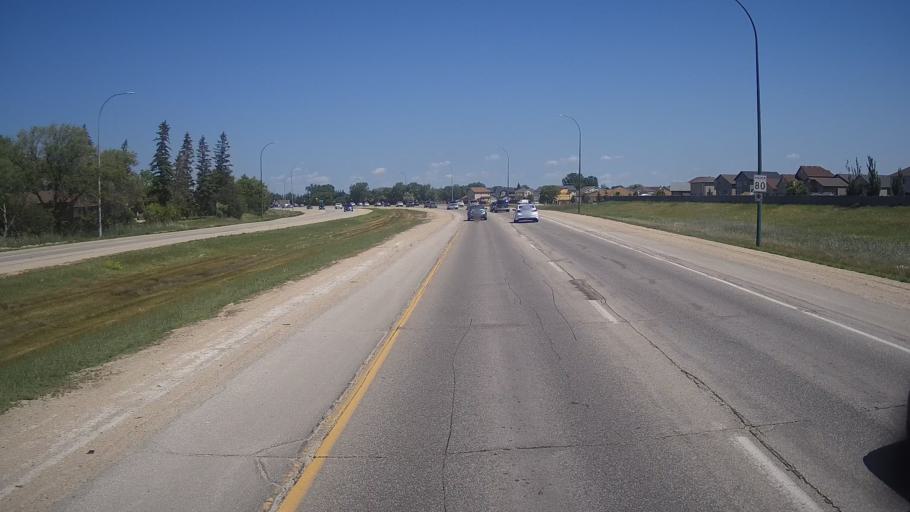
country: CA
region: Manitoba
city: Winnipeg
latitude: 49.9164
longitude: -97.0521
